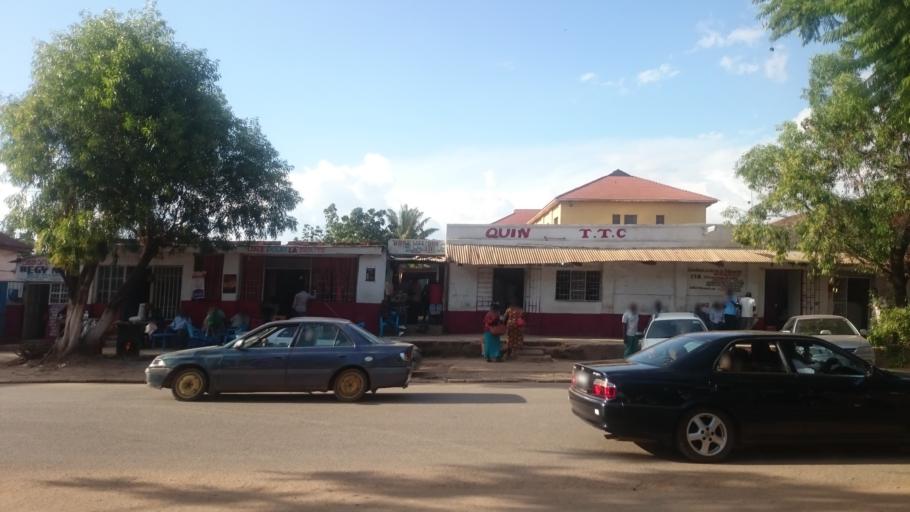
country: CD
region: Katanga
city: Lubumbashi
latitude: -11.6724
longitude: 27.4852
